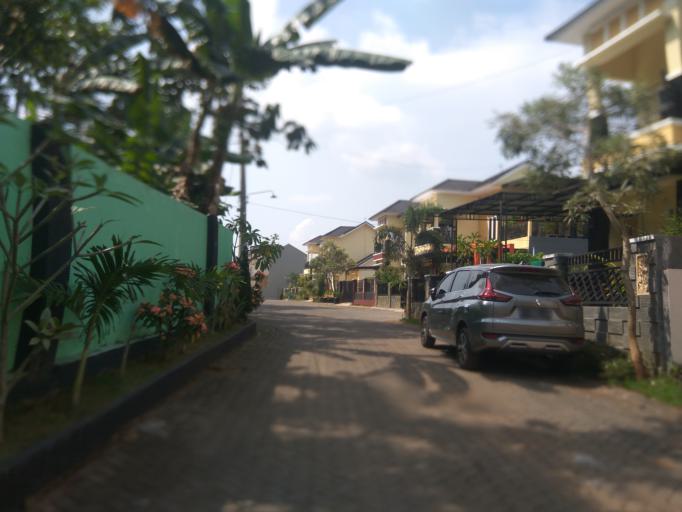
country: ID
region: Central Java
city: Ungaran
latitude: -7.0721
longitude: 110.4463
